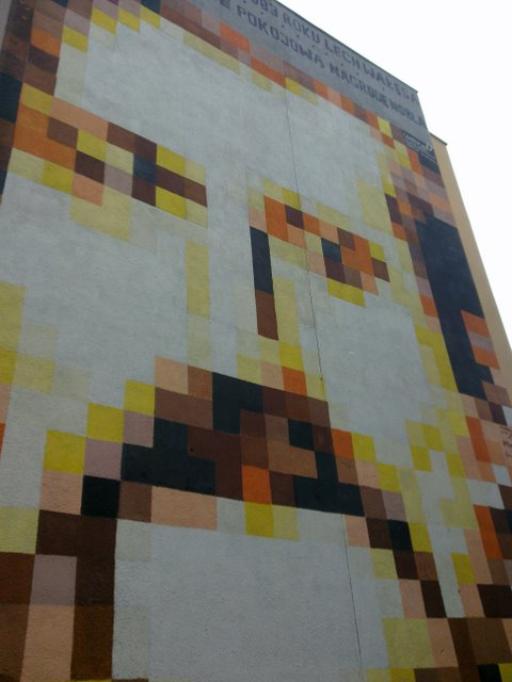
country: PL
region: Pomeranian Voivodeship
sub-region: Sopot
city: Sopot
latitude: 54.3953
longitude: 18.5908
